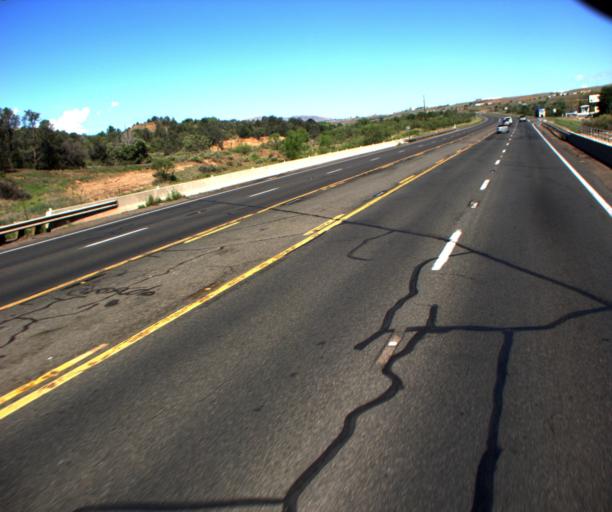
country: US
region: Arizona
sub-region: Yavapai County
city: Dewey-Humboldt
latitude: 34.5672
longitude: -112.2677
